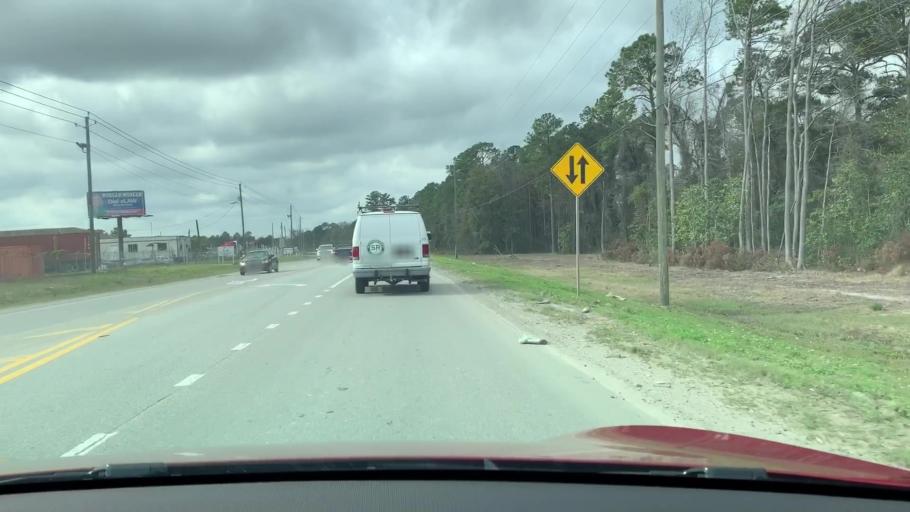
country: US
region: Georgia
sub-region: Chatham County
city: Port Wentworth
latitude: 32.1457
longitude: -81.1814
